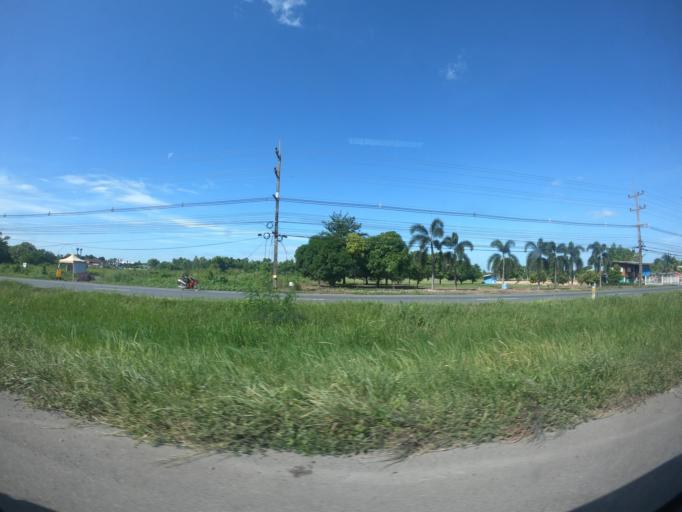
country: TH
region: Nakhon Nayok
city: Ban Na
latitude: 14.2468
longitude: 101.1072
